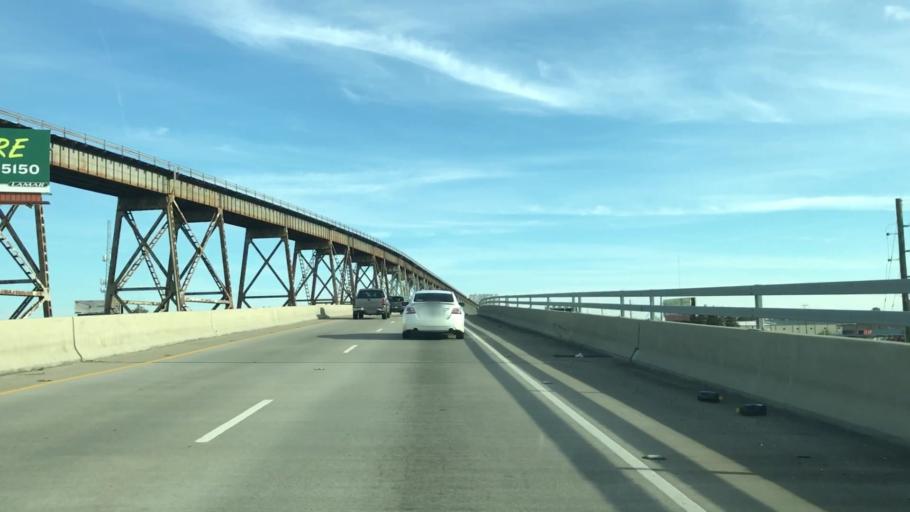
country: US
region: Louisiana
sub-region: Jefferson Parish
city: Elmwood
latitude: 29.9539
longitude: -90.1805
